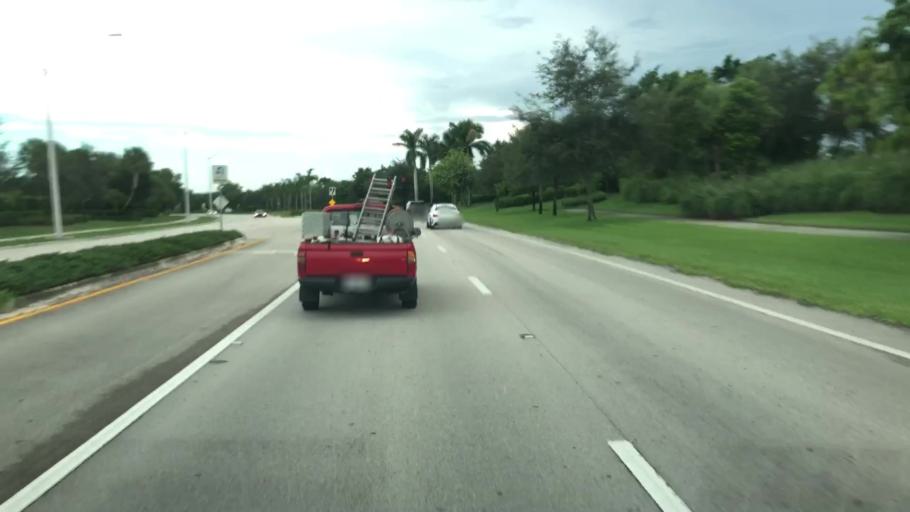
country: US
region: Florida
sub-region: Broward County
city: Parkland
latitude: 26.3226
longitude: -80.2785
